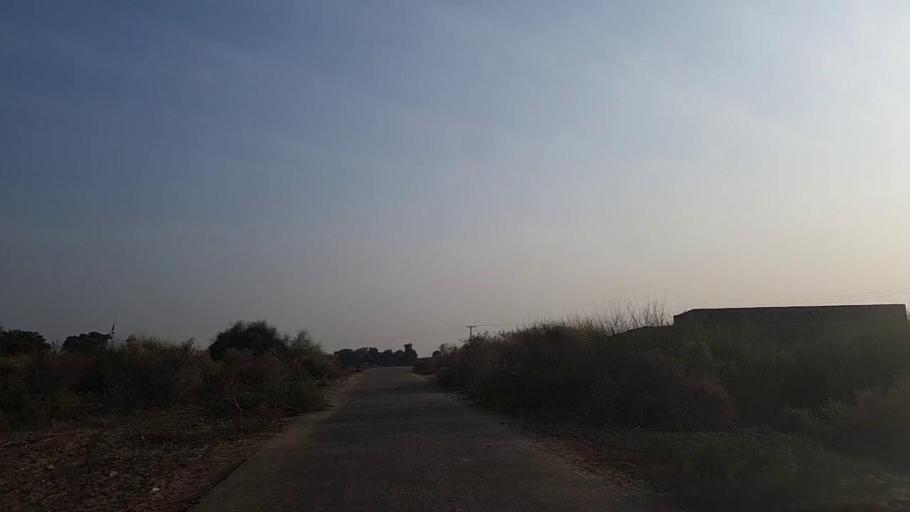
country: PK
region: Sindh
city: Jam Sahib
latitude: 26.4350
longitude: 68.5931
